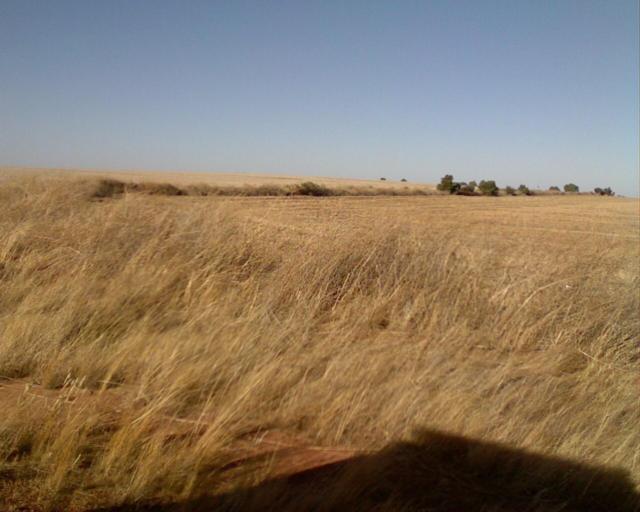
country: AU
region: Western Australia
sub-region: Moora
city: Moora
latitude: -30.2609
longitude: 116.3836
